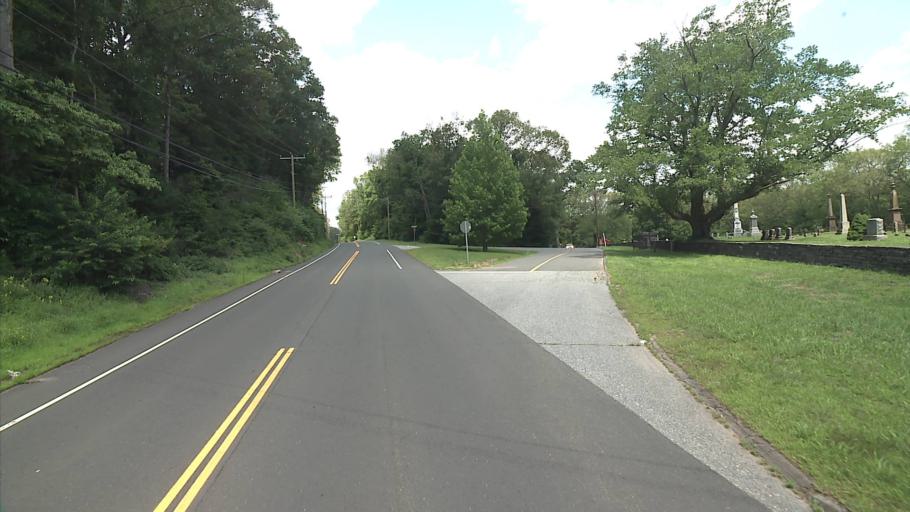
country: US
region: Connecticut
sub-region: Middlesex County
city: East Haddam
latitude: 41.4556
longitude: -72.4796
